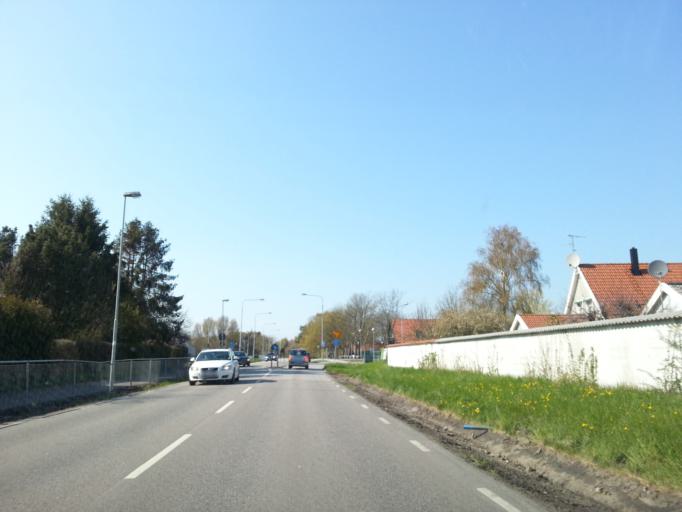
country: SE
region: Skane
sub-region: Vellinge Kommun
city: Hollviken
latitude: 55.4137
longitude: 12.9758
